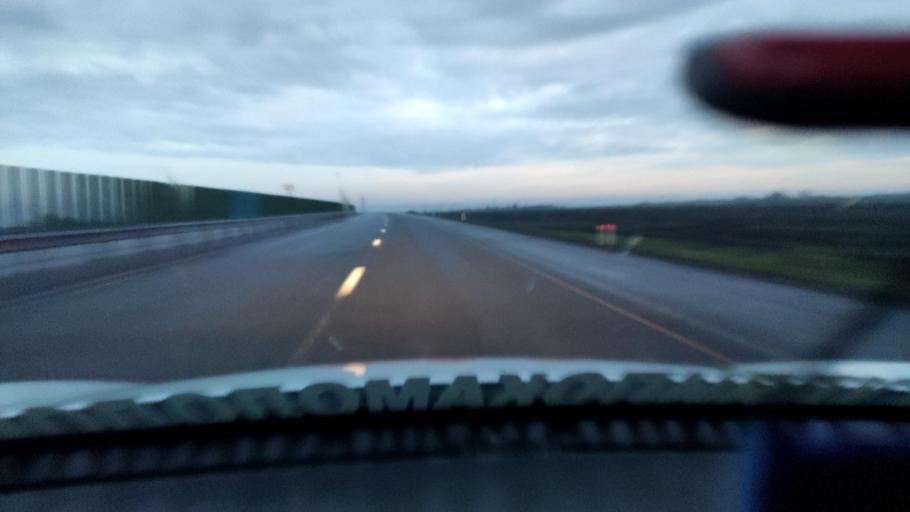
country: RU
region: Rostov
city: Tarasovskiy
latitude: 48.7427
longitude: 40.3944
